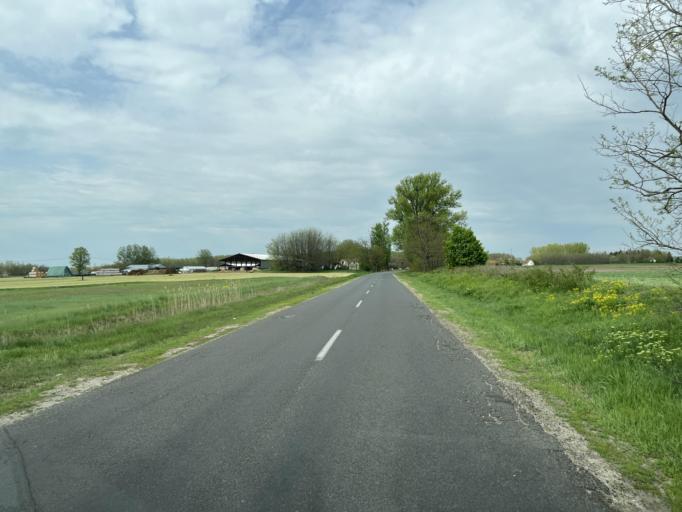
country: HU
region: Pest
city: Tortel
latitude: 47.1399
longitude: 19.8866
